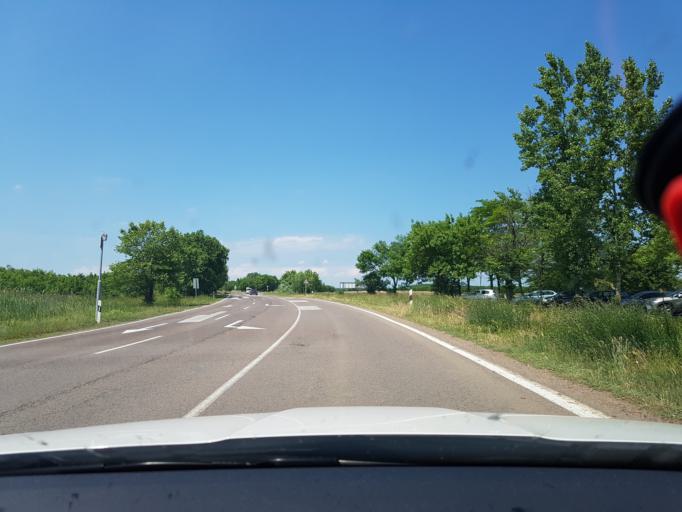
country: HU
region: Hajdu-Bihar
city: Egyek
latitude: 47.5911
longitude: 20.8519
